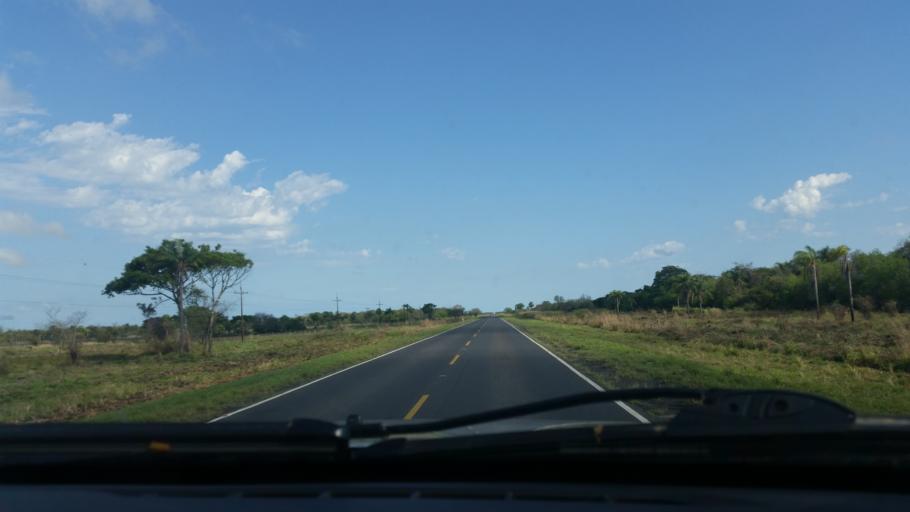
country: PY
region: Presidente Hayes
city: Benjamin Aceval
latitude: -24.9015
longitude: -57.6546
